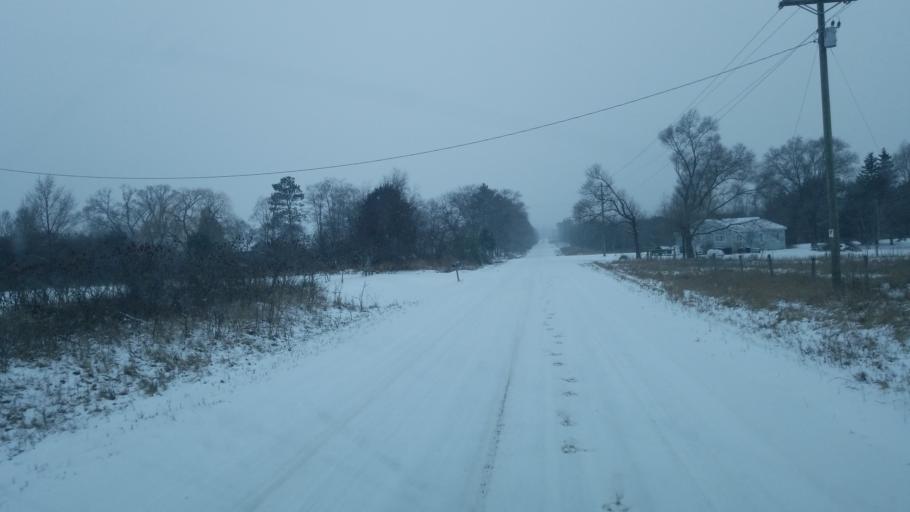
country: US
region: Michigan
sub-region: Osceola County
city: Reed City
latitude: 43.8290
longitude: -85.4124
